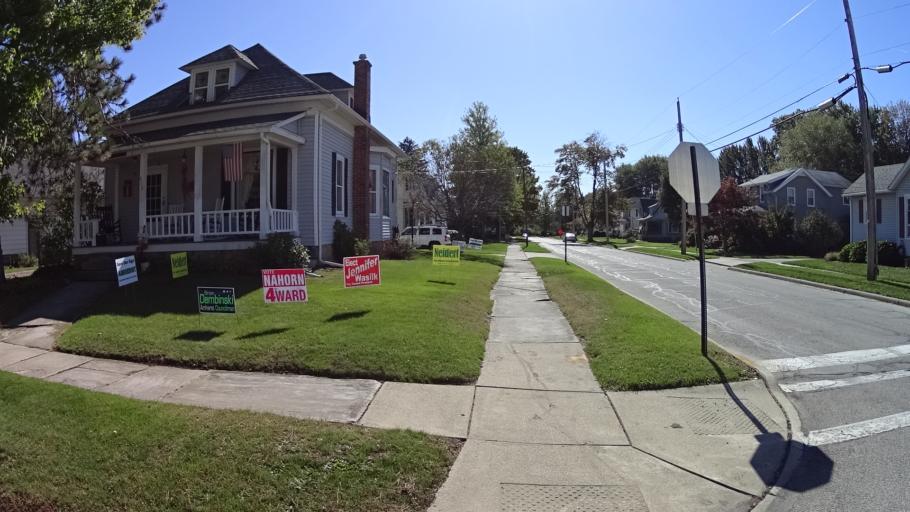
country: US
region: Ohio
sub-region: Lorain County
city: Amherst
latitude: 41.3950
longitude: -82.2234
